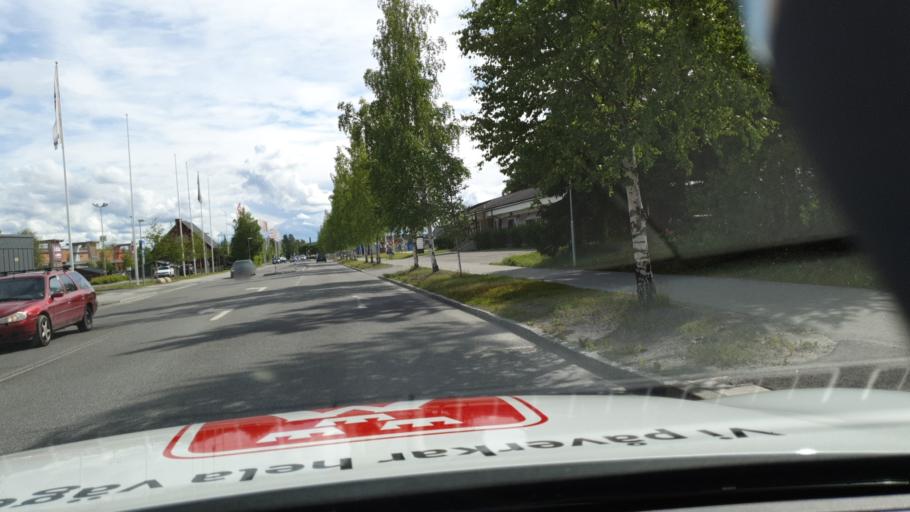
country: SE
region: Jaemtland
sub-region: OEstersunds Kommun
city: Ostersund
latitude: 63.1729
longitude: 14.6902
